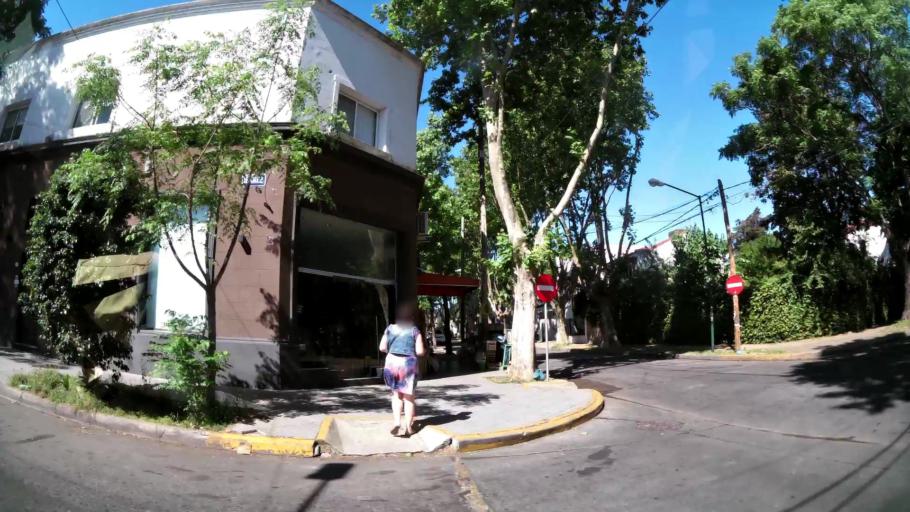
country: AR
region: Buenos Aires
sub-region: Partido de San Isidro
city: San Isidro
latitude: -34.4643
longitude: -58.5205
